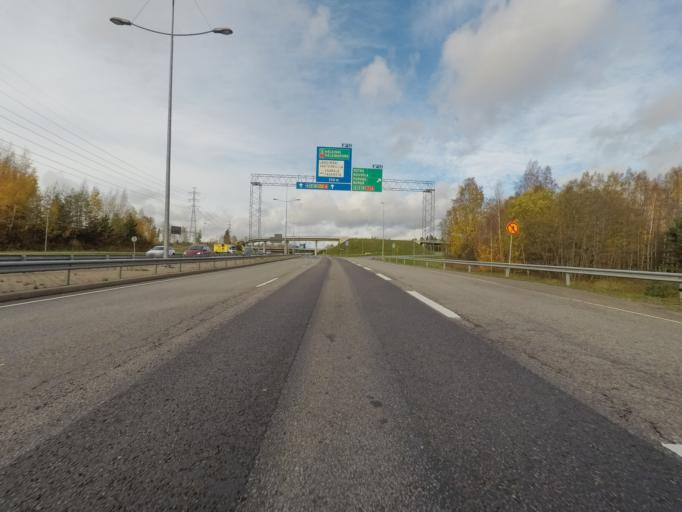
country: FI
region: Uusimaa
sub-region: Helsinki
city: Vantaa
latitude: 60.2551
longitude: 25.1298
